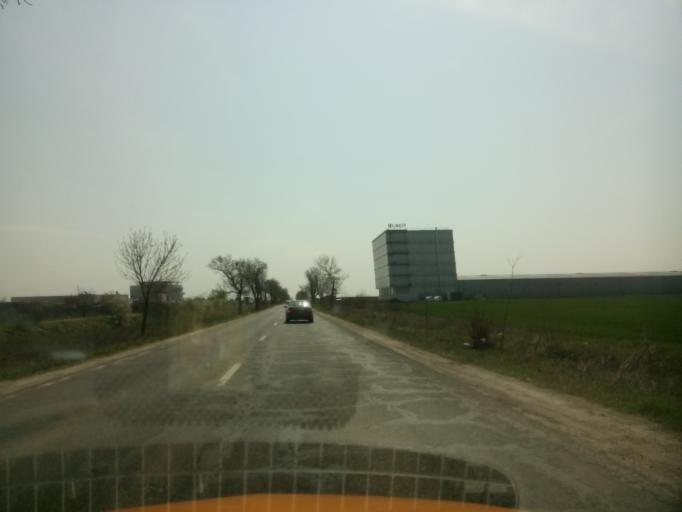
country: RO
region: Ilfov
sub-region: Comuna Glina
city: Glina
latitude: 44.3424
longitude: 26.2311
